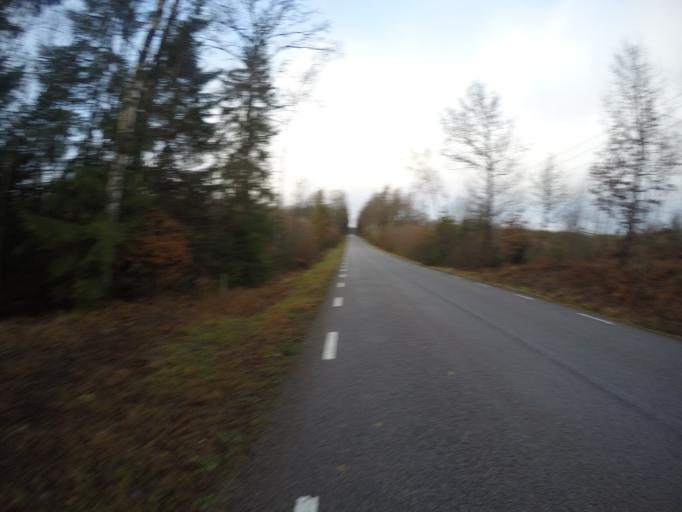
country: SE
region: Skane
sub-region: Osby Kommun
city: Lonsboda
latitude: 56.3807
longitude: 14.3409
